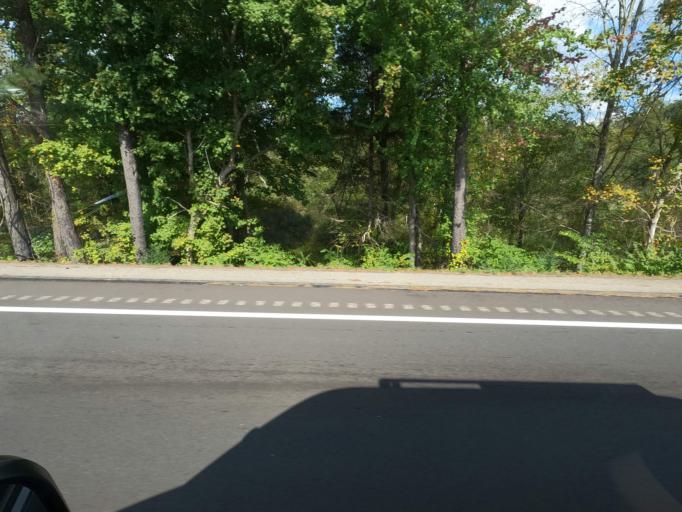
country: US
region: Tennessee
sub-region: Loudon County
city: Lenoir City
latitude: 35.8344
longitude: -84.2885
